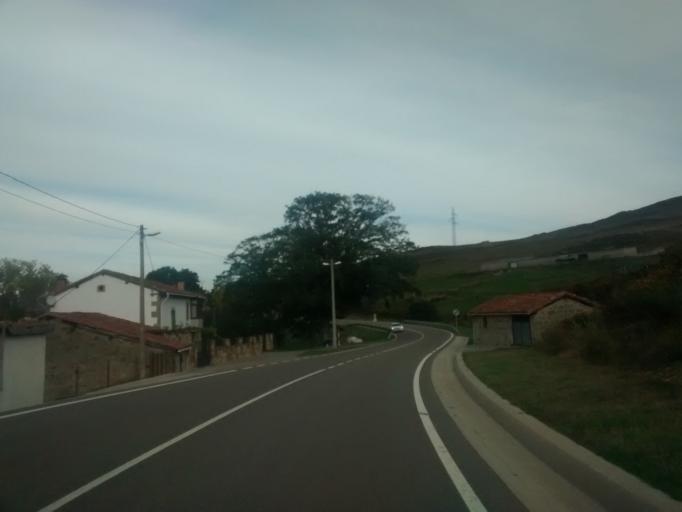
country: ES
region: Castille and Leon
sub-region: Provincia de Burgos
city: Arija
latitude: 42.9744
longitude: -4.0045
